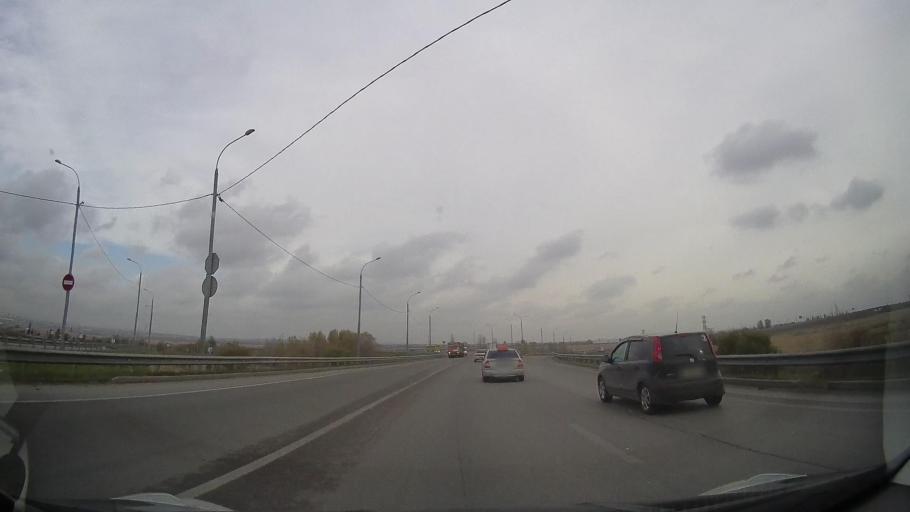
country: RU
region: Rostov
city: Bataysk
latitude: 47.1668
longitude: 39.7440
